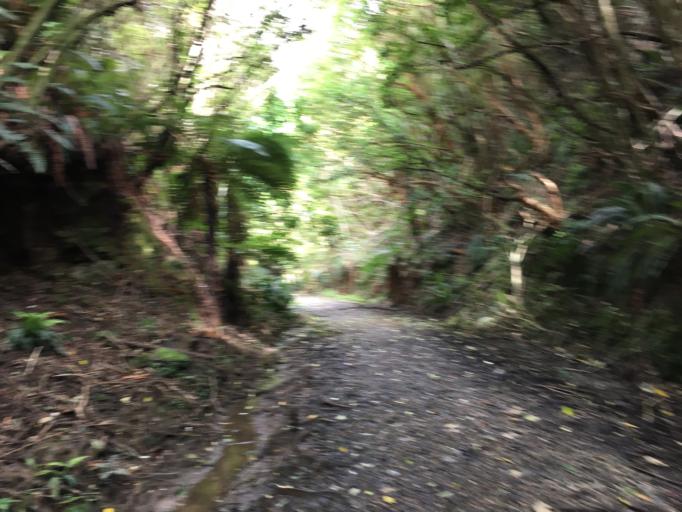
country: NZ
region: Otago
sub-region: Clutha District
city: Papatowai
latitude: -46.4961
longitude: 169.4811
